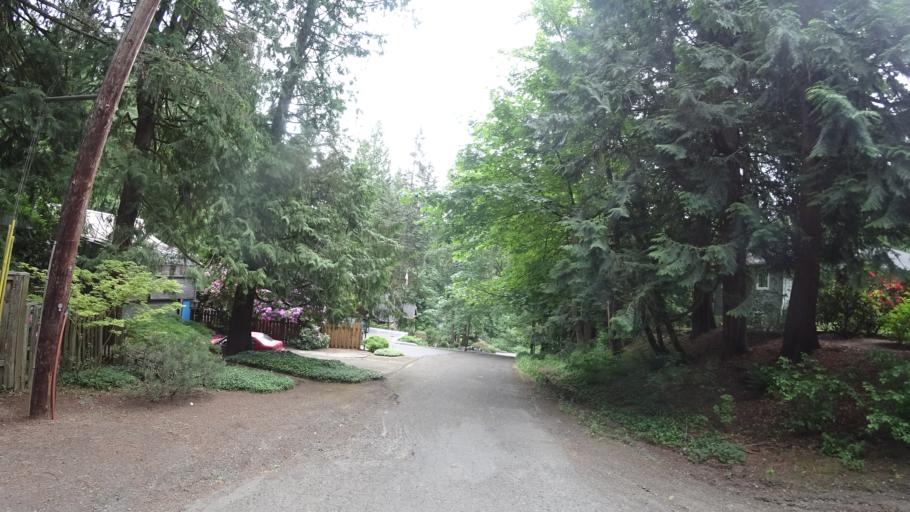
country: US
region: Oregon
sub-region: Clackamas County
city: Lake Oswego
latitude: 45.4438
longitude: -122.7106
